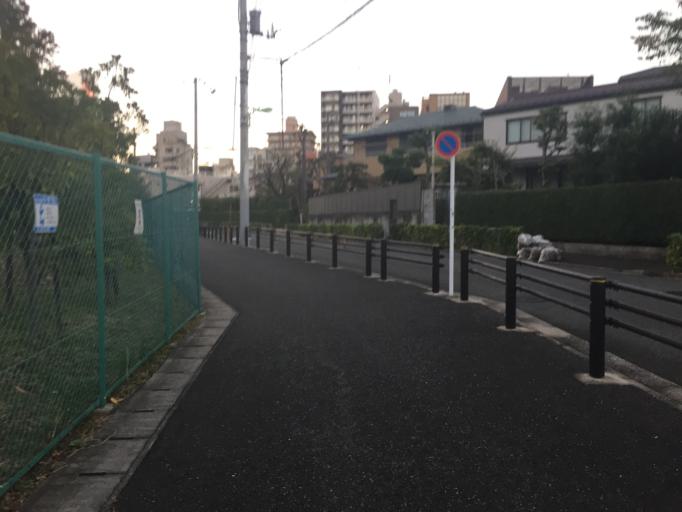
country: JP
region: Tokyo
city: Tokyo
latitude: 35.6298
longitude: 139.6593
